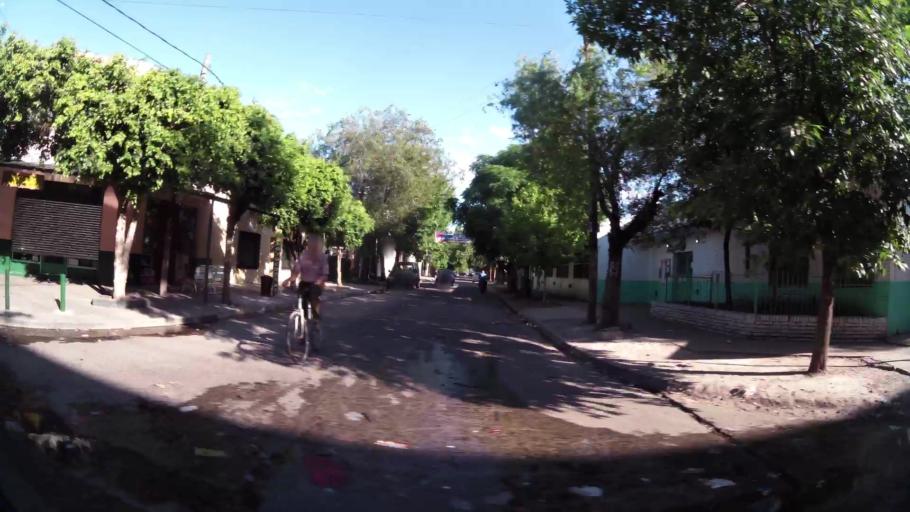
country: AR
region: Buenos Aires
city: Santa Catalina - Dique Lujan
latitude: -34.4900
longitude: -58.7256
